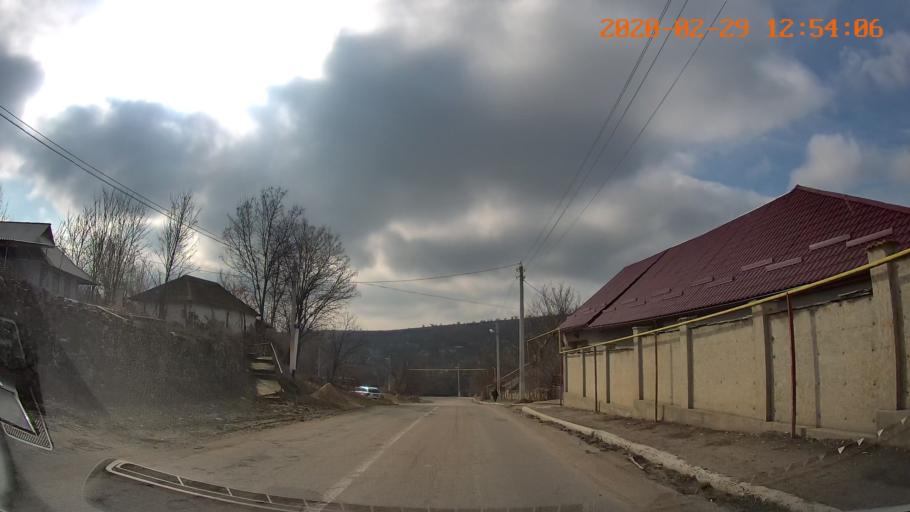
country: MD
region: Telenesti
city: Camenca
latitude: 48.1044
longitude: 28.7291
